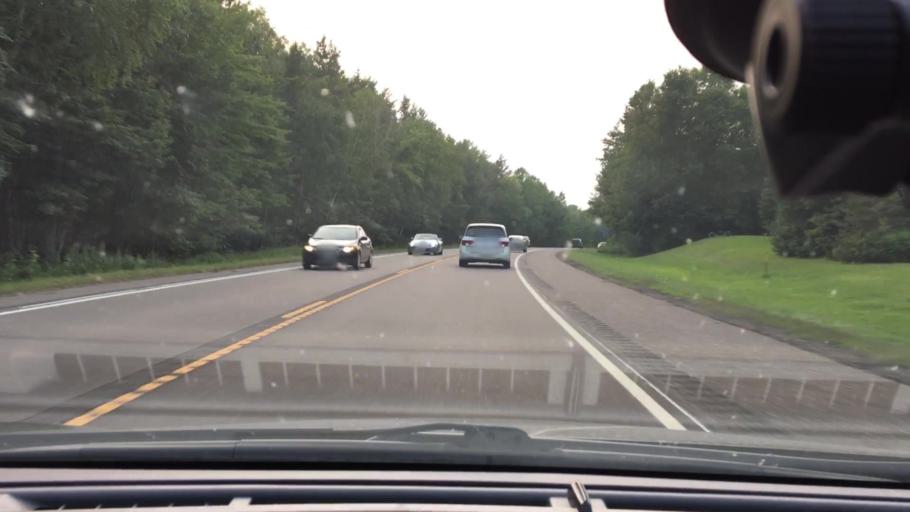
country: US
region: Minnesota
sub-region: Mille Lacs County
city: Vineland
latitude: 46.1299
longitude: -93.6853
